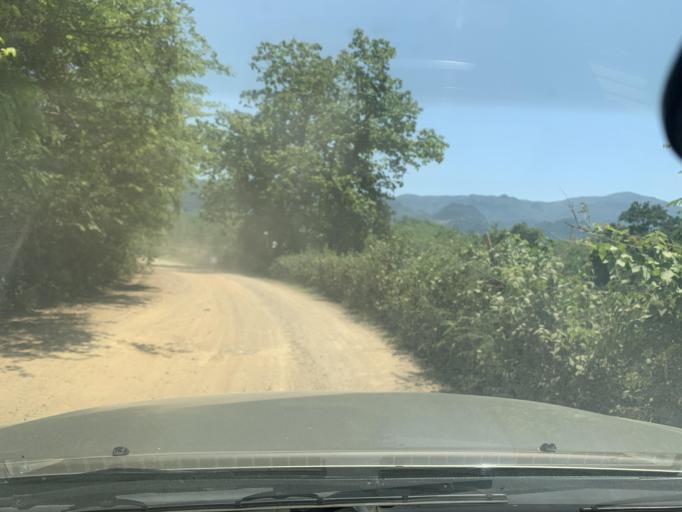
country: LA
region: Louangphabang
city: Louangphabang
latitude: 19.9059
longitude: 102.2382
